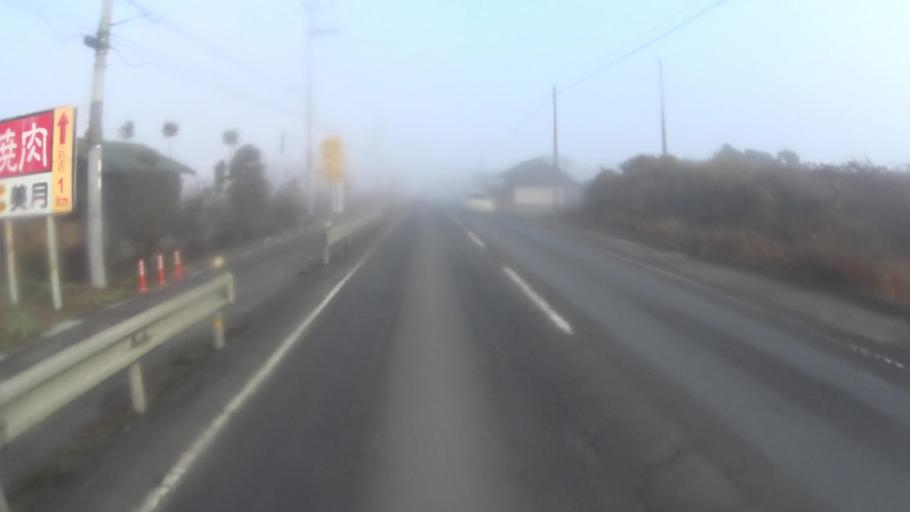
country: JP
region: Kyoto
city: Ayabe
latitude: 35.1696
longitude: 135.4243
